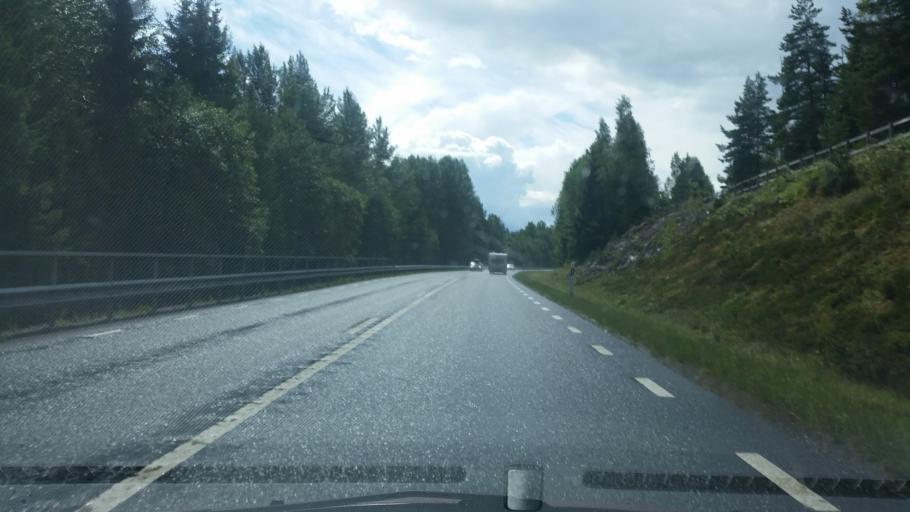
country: SE
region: Joenkoeping
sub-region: Gislaveds Kommun
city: Gislaved
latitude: 57.3757
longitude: 13.5776
